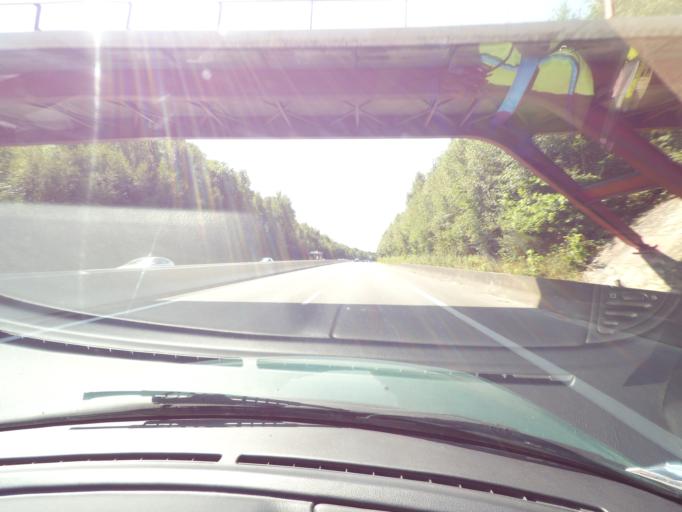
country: FR
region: Limousin
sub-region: Departement de la Haute-Vienne
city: Le Palais-sur-Vienne
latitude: 45.8668
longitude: 1.2875
